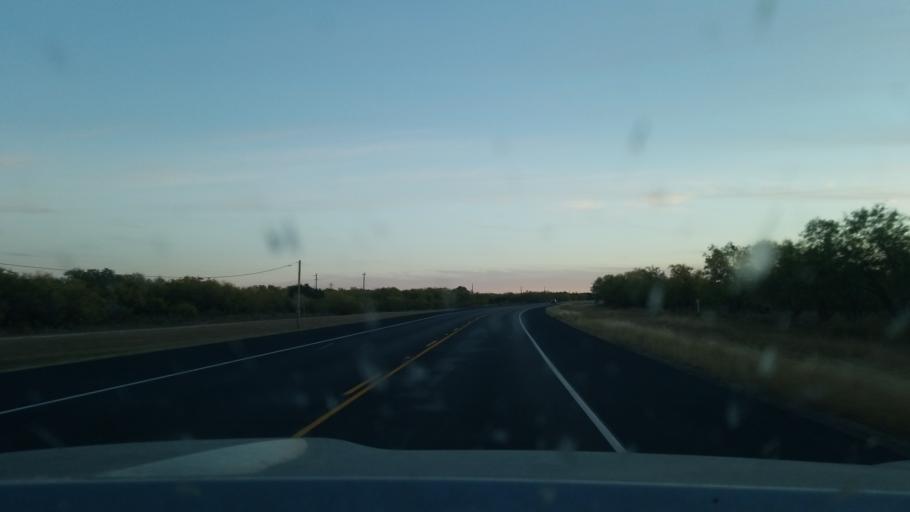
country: US
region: Texas
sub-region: Stephens County
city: Breckenridge
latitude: 32.6127
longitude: -98.9003
